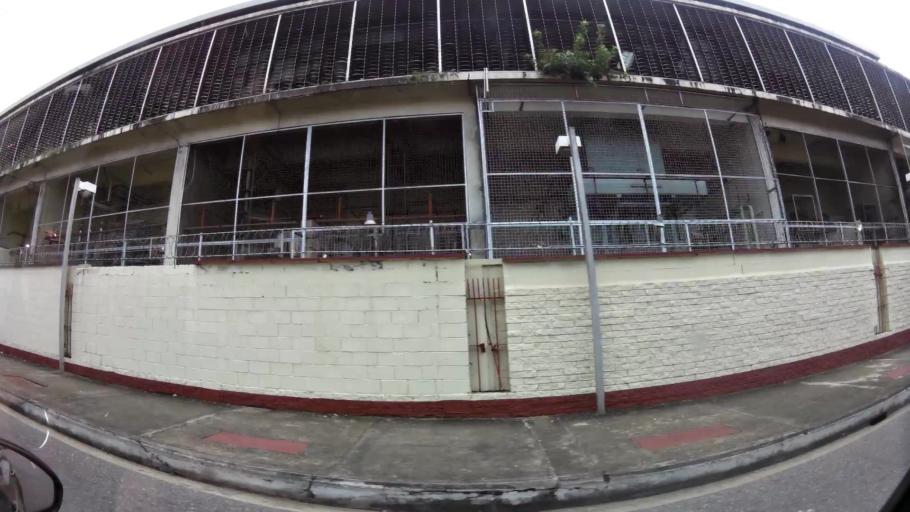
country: TT
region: City of Port of Spain
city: Port-of-Spain
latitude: 10.6568
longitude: -61.5190
